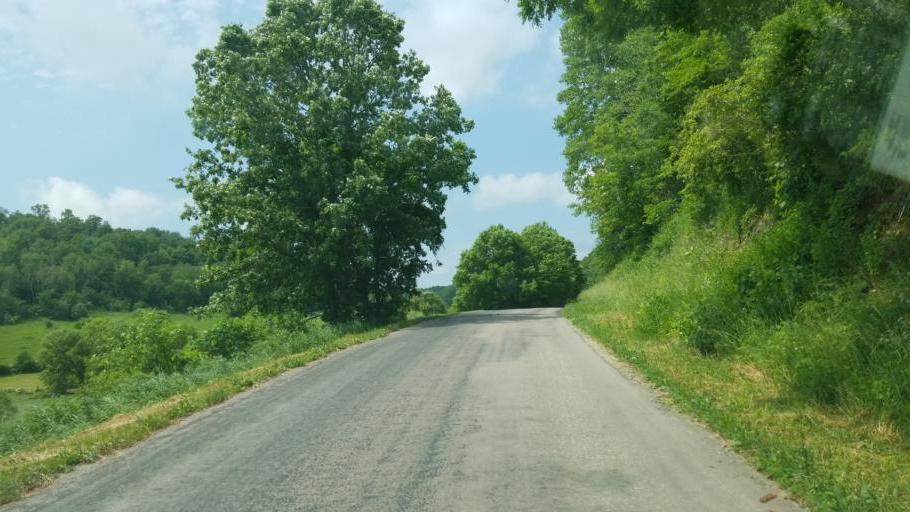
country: US
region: Wisconsin
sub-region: Monroe County
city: Cashton
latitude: 43.7182
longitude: -90.6818
